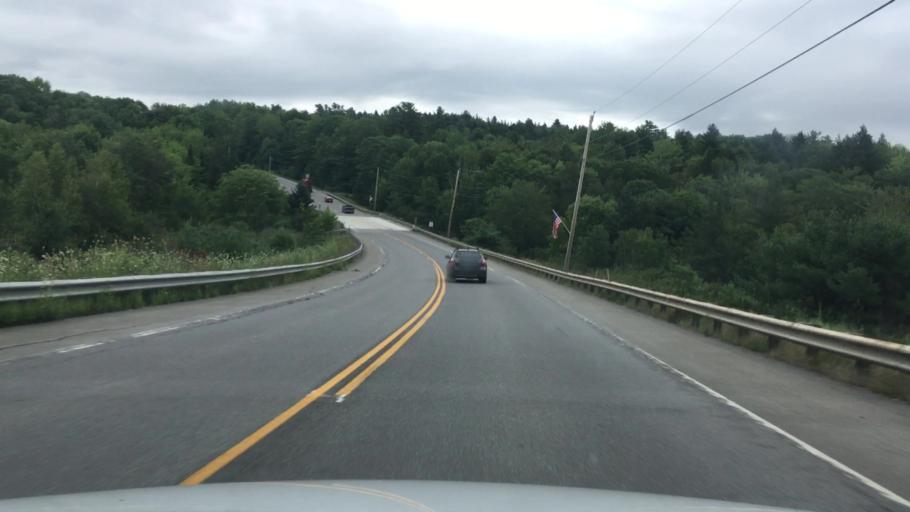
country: US
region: Maine
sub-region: Penobscot County
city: Bradley
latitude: 44.8268
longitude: -68.3776
